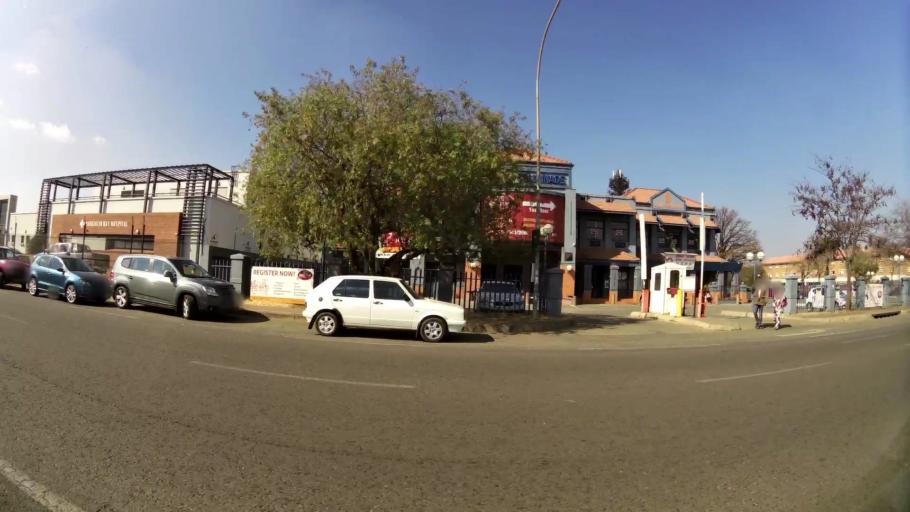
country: ZA
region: Gauteng
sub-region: City of Johannesburg Metropolitan Municipality
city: Modderfontein
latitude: -26.1020
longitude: 28.2330
